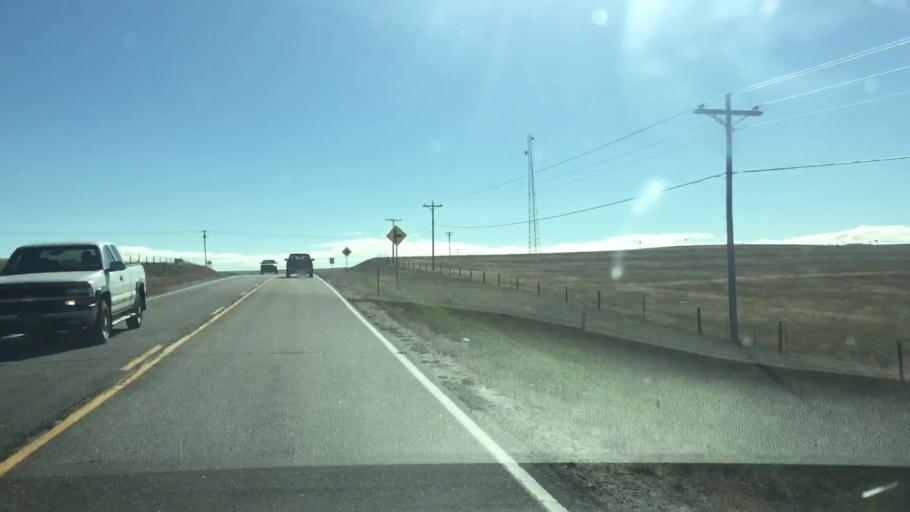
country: US
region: Colorado
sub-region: Elbert County
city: Kiowa
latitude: 39.3490
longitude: -104.4811
